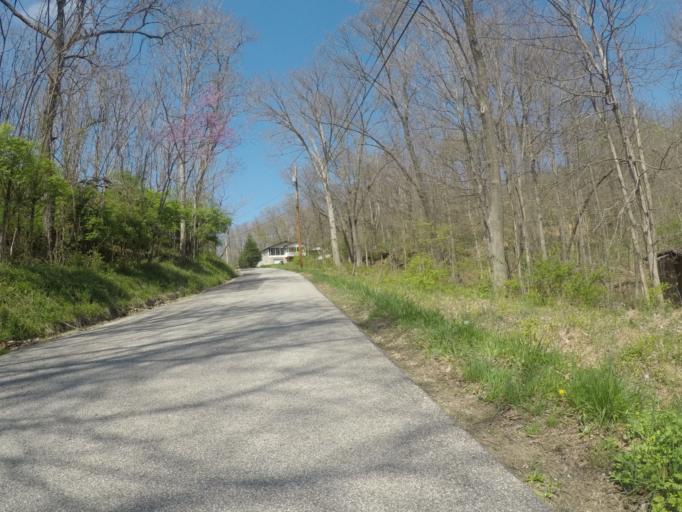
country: US
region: Ohio
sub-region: Lawrence County
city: Burlington
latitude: 38.3817
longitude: -82.5326
